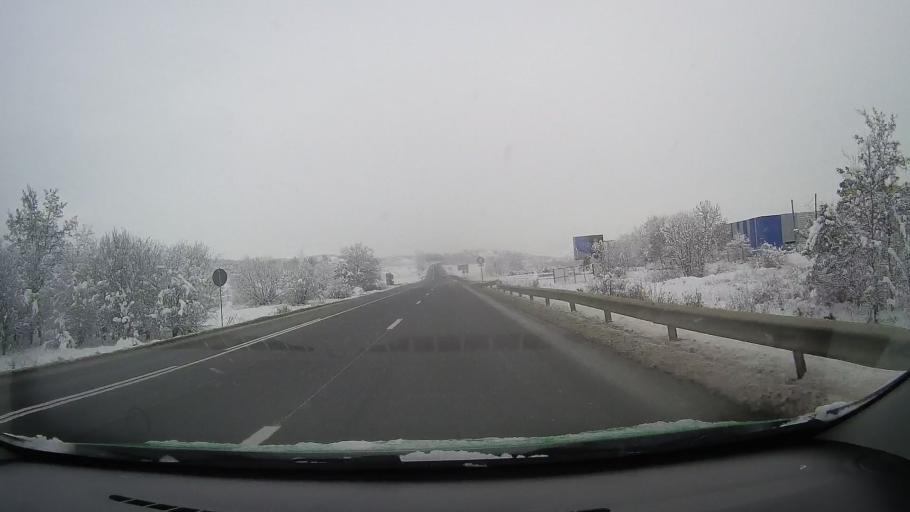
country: RO
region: Sibiu
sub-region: Comuna Cristian
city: Cristian
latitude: 45.7886
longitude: 24.0496
